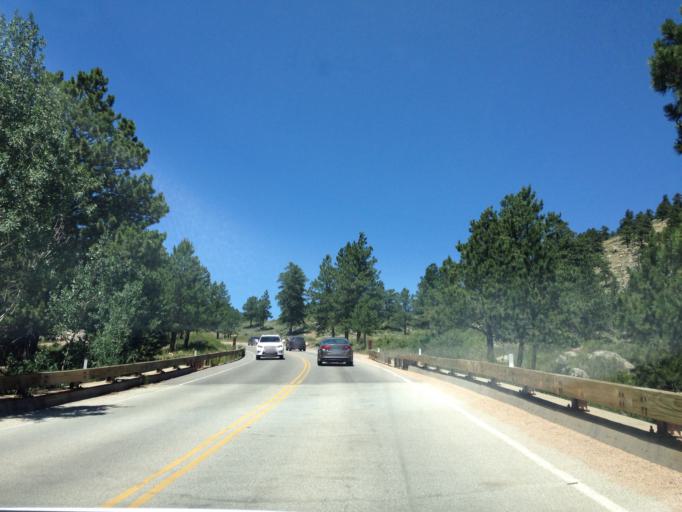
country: US
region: Colorado
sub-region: Larimer County
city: Estes Park
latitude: 40.3507
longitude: -105.5778
